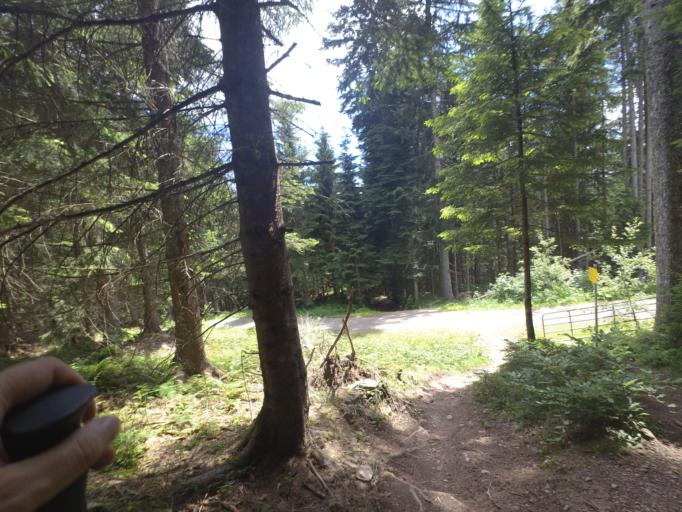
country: AT
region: Salzburg
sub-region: Politischer Bezirk Zell am See
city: Leogang
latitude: 47.4557
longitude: 12.7695
